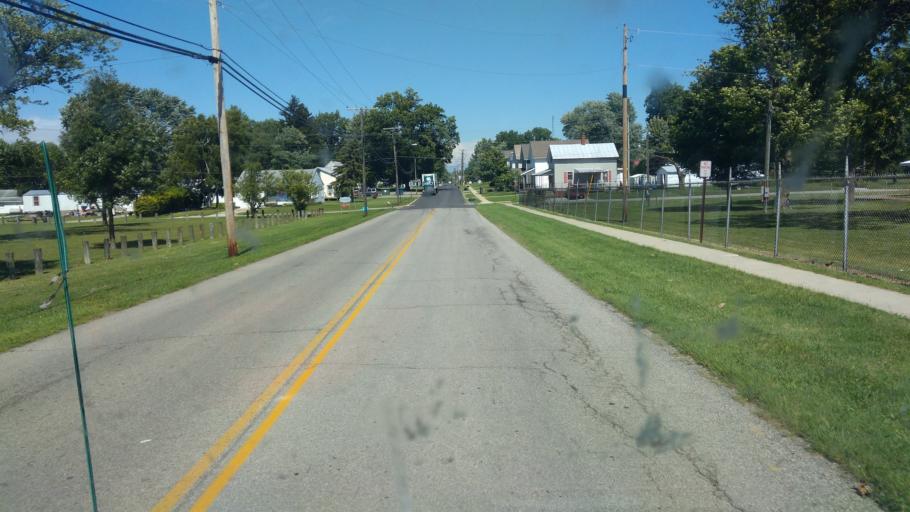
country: US
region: Ohio
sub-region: Crawford County
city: Bucyrus
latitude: 40.8025
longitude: -82.9590
